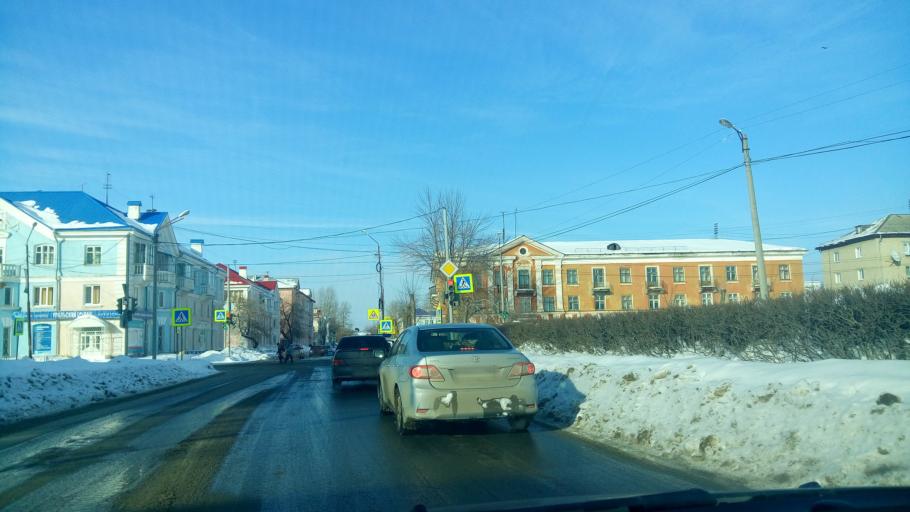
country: RU
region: Sverdlovsk
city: Bogdanovich
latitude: 56.7738
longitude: 62.0553
